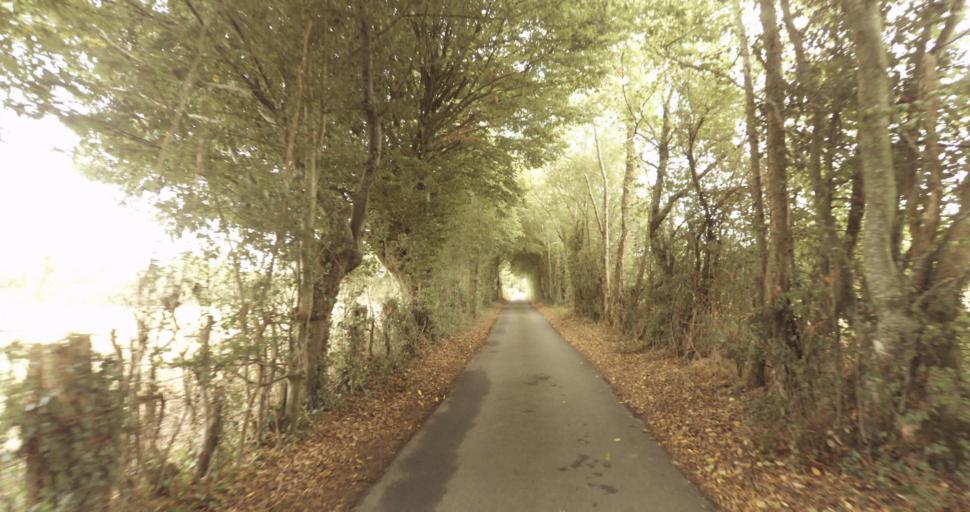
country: FR
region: Lower Normandy
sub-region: Departement de l'Orne
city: Gace
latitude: 48.8669
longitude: 0.3141
